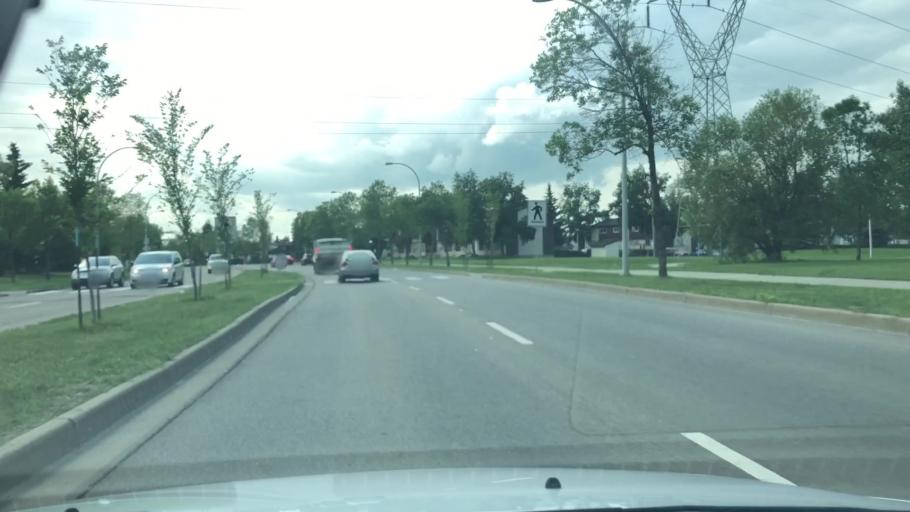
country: CA
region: Alberta
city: Edmonton
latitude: 53.6165
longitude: -113.5280
